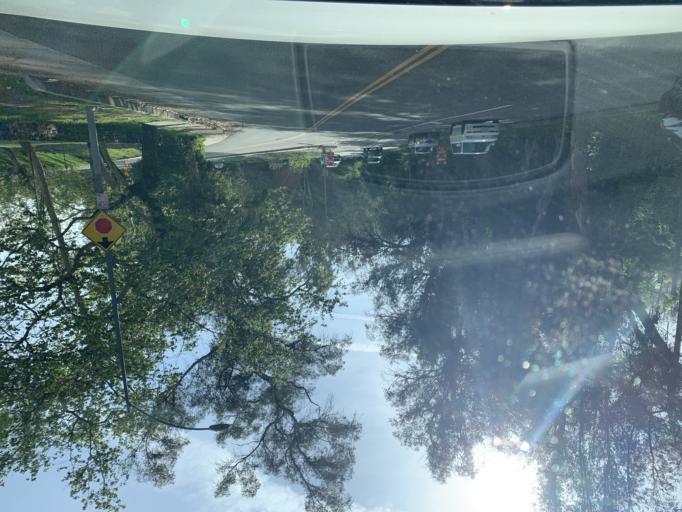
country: US
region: California
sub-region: Los Angeles County
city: South Pasadena
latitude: 34.1106
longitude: -118.1786
